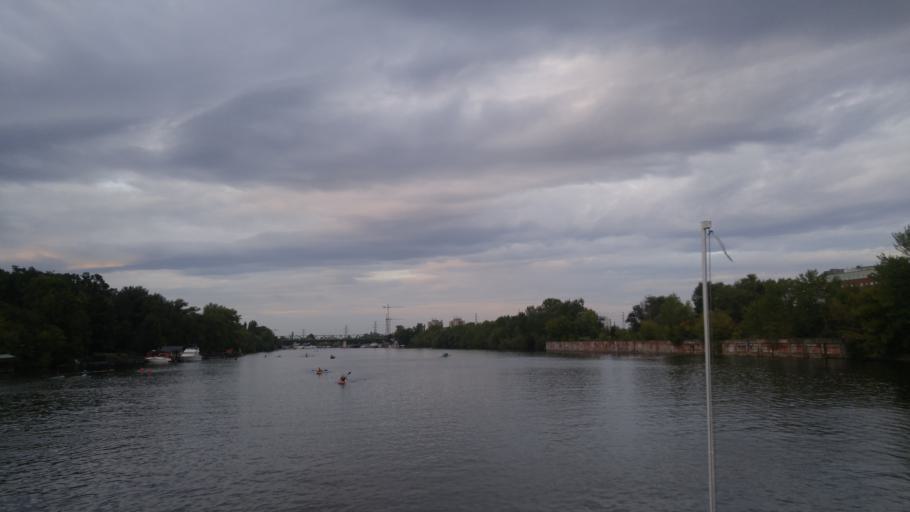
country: HU
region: Budapest
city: Budapest IV. keruelet
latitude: 47.5526
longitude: 19.0701
